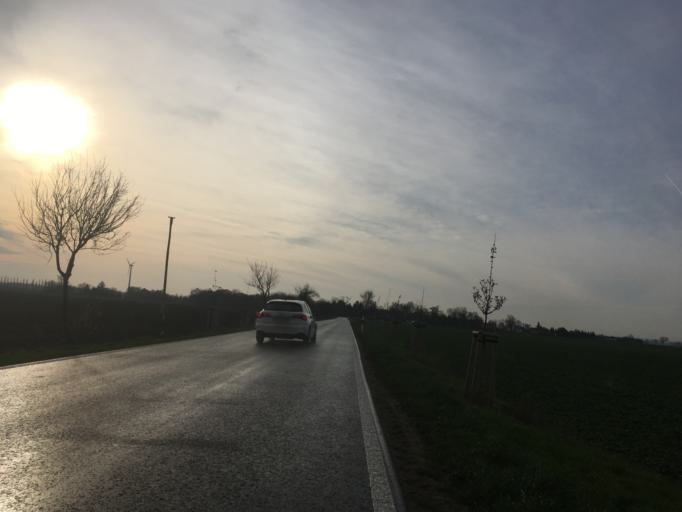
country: DE
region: Brandenburg
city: Neulewin
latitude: 52.7653
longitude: 14.2218
